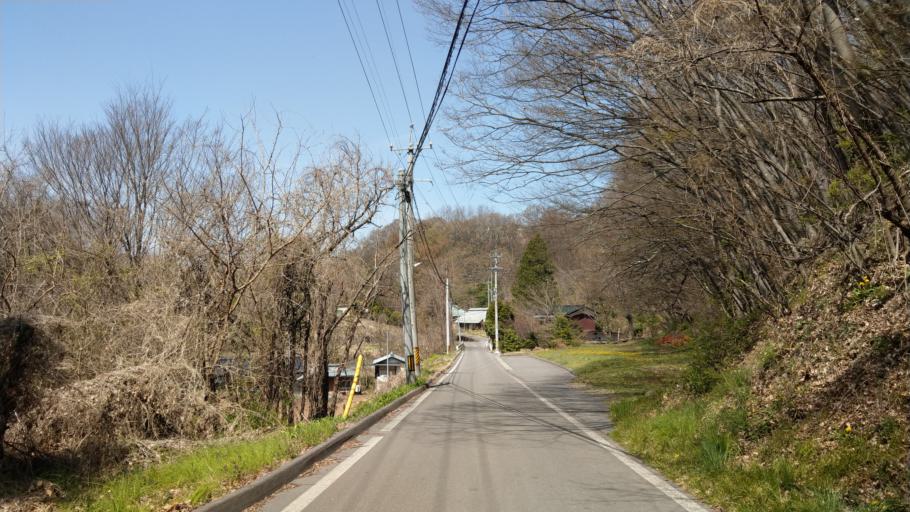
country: JP
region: Nagano
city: Komoro
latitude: 36.3358
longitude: 138.4017
